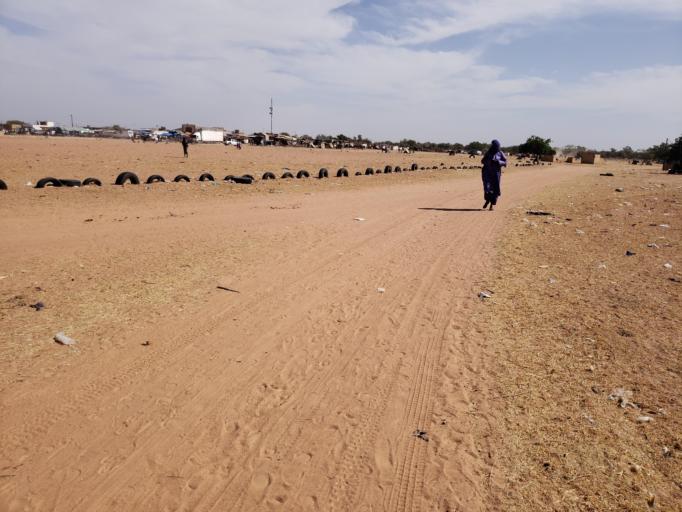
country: SN
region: Matam
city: Ranerou
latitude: 15.2973
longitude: -13.9634
